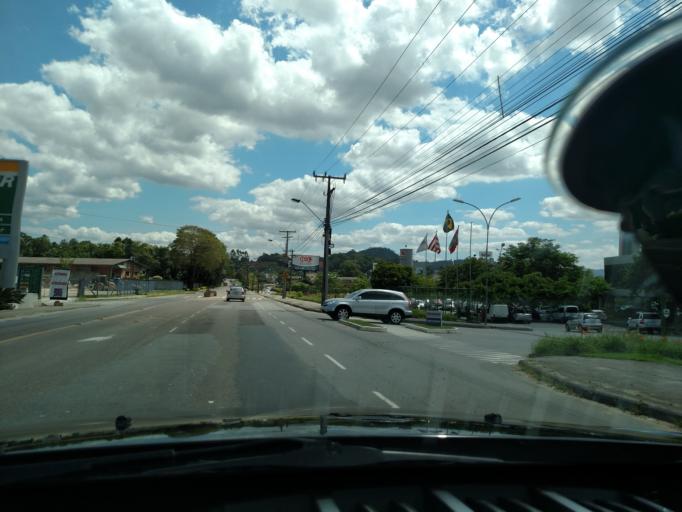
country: BR
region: Santa Catarina
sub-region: Blumenau
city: Blumenau
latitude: -26.8725
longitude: -49.0992
